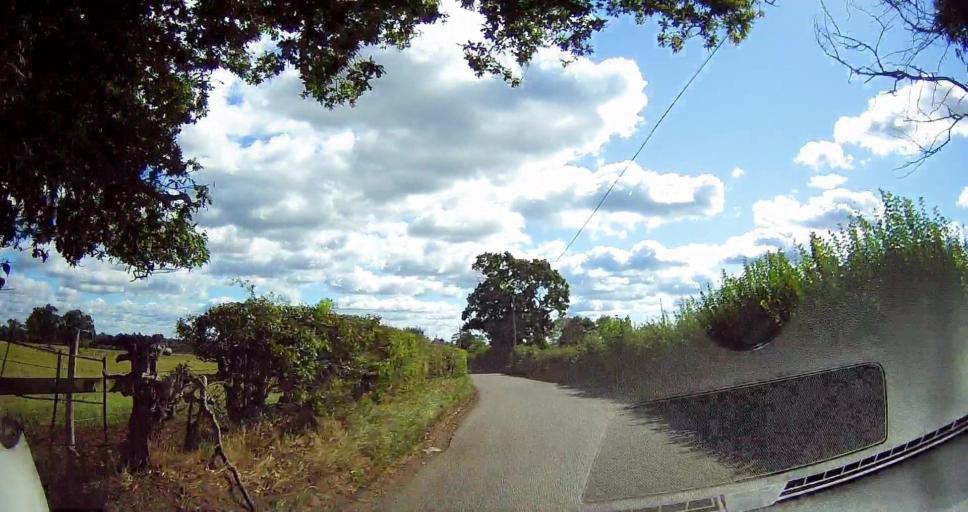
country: GB
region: England
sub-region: Cheshire East
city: Nantwich
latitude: 52.9855
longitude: -2.5323
